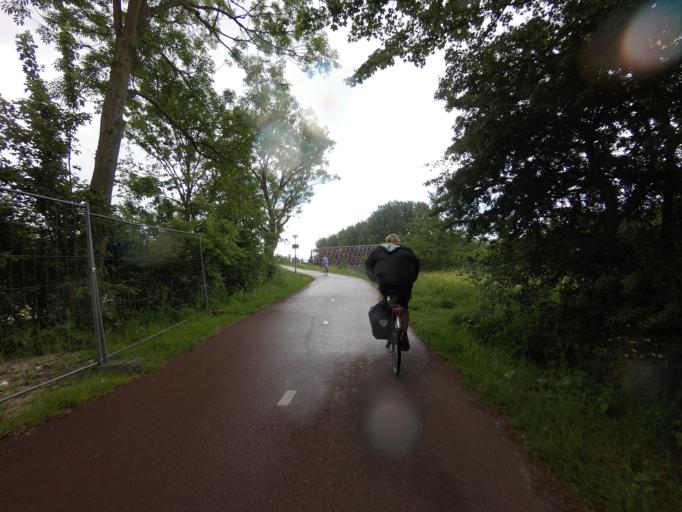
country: NL
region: South Holland
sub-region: Gemeente Vlaardingen
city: Vlaardingen
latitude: 51.9238
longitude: 4.3404
